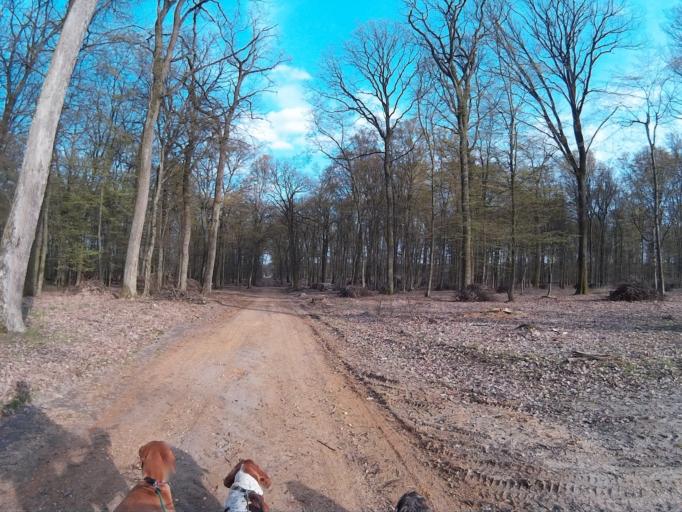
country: HU
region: Vas
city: Sarvar
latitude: 47.1940
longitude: 16.9971
